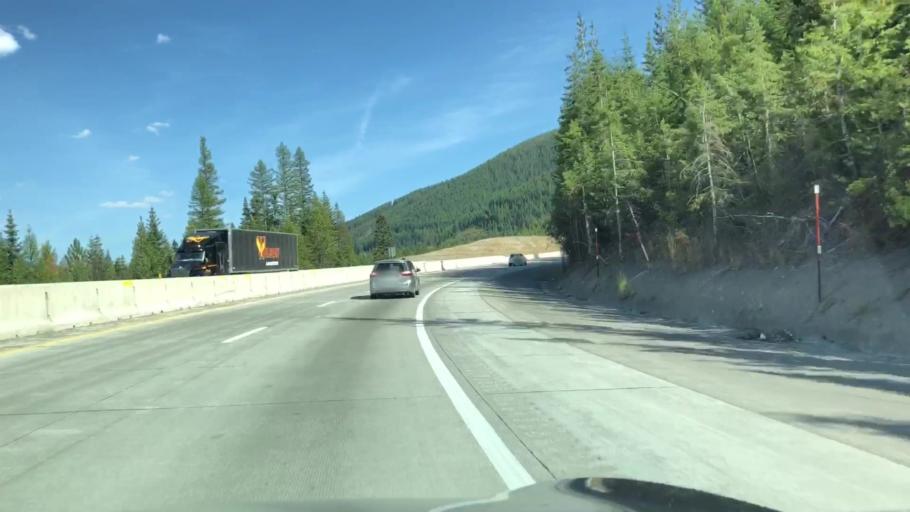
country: US
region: Idaho
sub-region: Shoshone County
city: Wallace
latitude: 47.4628
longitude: -115.7402
